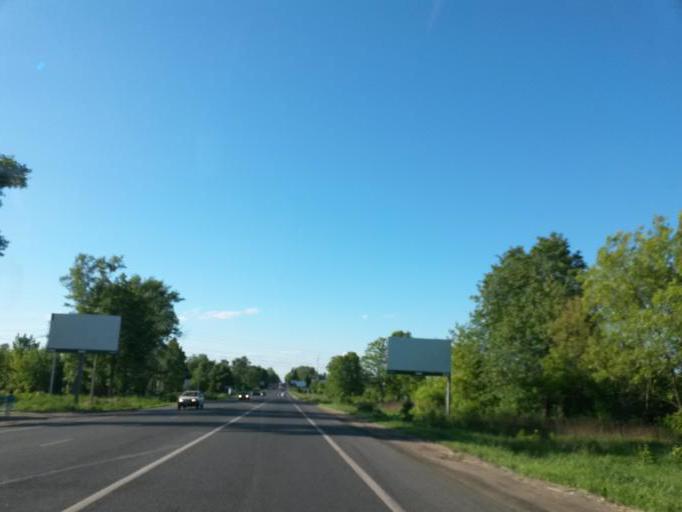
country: RU
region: Moskovskaya
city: L'vovskiy
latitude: 55.3077
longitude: 37.5289
